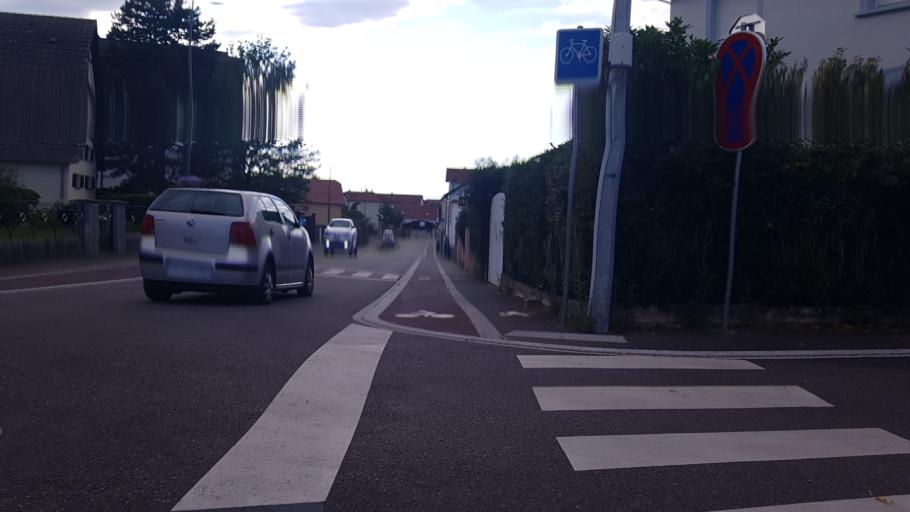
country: FR
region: Alsace
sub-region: Departement du Bas-Rhin
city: Brumath
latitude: 48.7277
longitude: 7.7200
